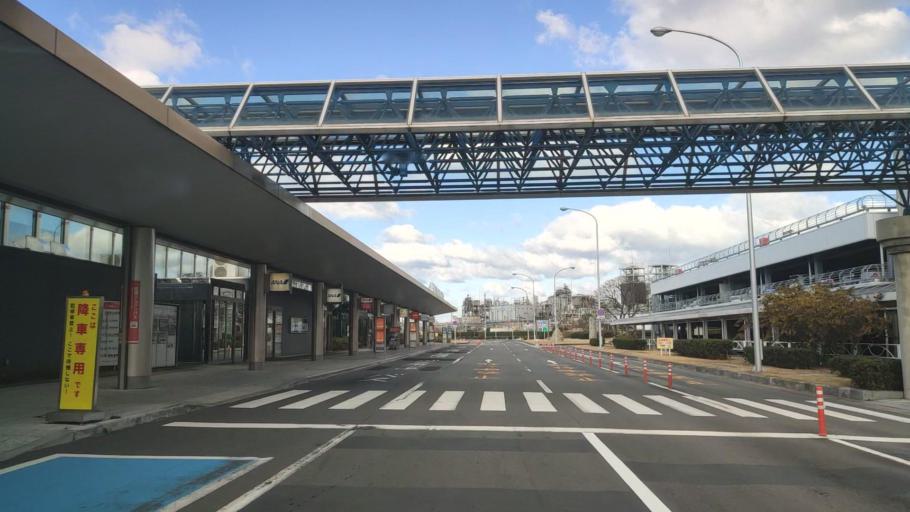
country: JP
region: Ehime
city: Masaki-cho
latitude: 33.8292
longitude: 132.7046
